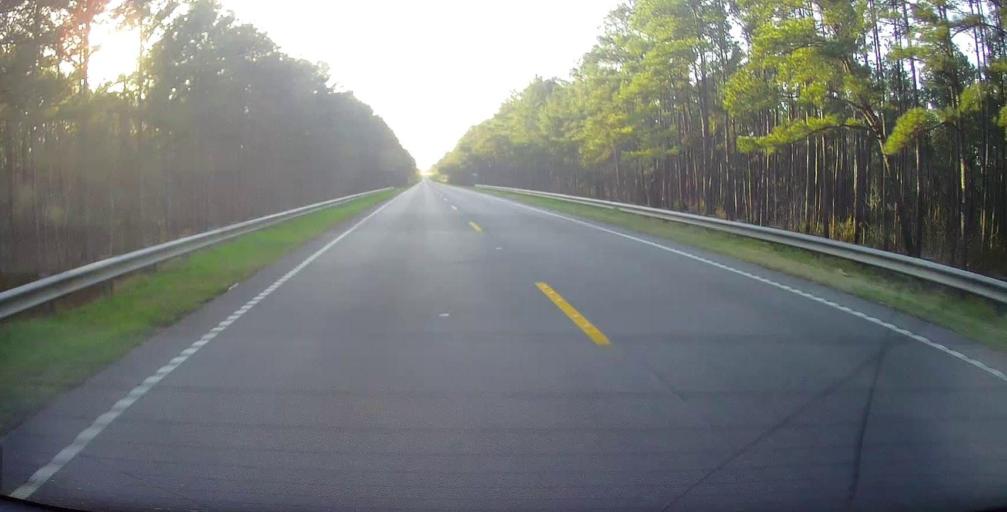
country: US
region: Georgia
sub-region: Evans County
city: Claxton
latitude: 32.1489
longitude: -81.7855
